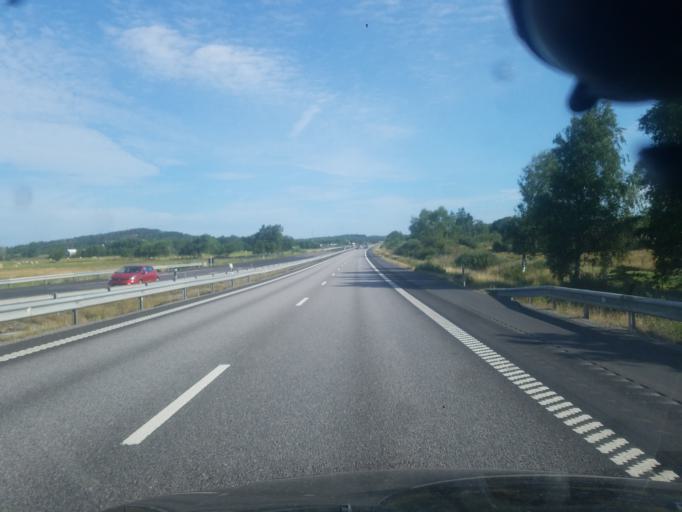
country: SE
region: Vaestra Goetaland
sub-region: Stenungsunds Kommun
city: Stora Hoga
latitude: 58.0104
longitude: 11.8433
